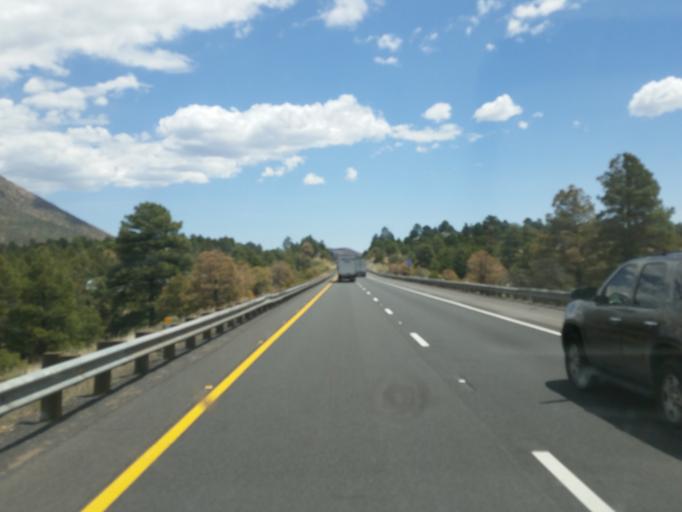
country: US
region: Arizona
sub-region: Coconino County
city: Flagstaff
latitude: 35.1969
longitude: -111.6143
